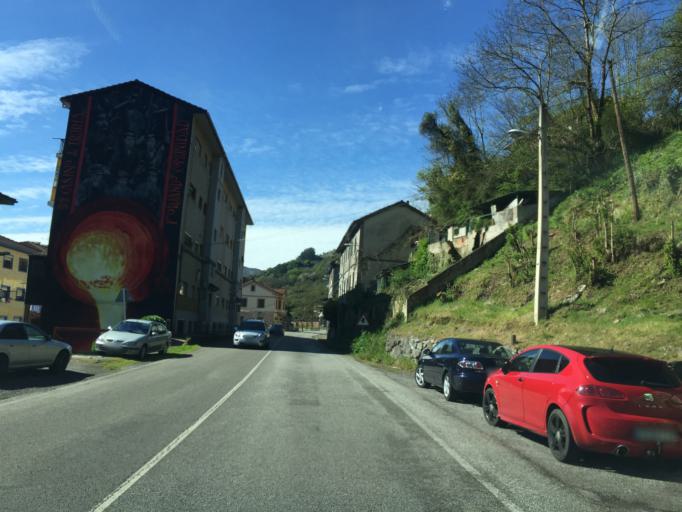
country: ES
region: Asturias
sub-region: Province of Asturias
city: Proaza
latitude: 43.3402
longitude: -5.9843
